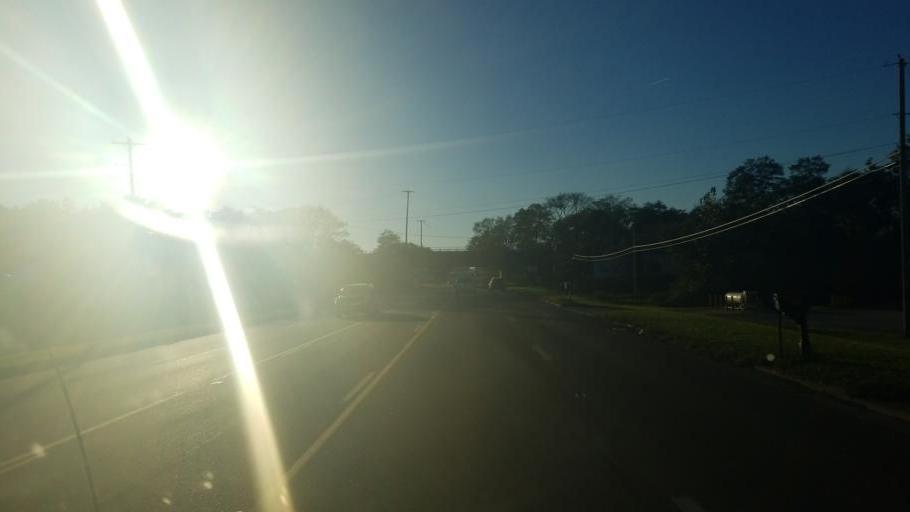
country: US
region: Ohio
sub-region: Stark County
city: Alliance
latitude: 40.9016
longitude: -81.0750
